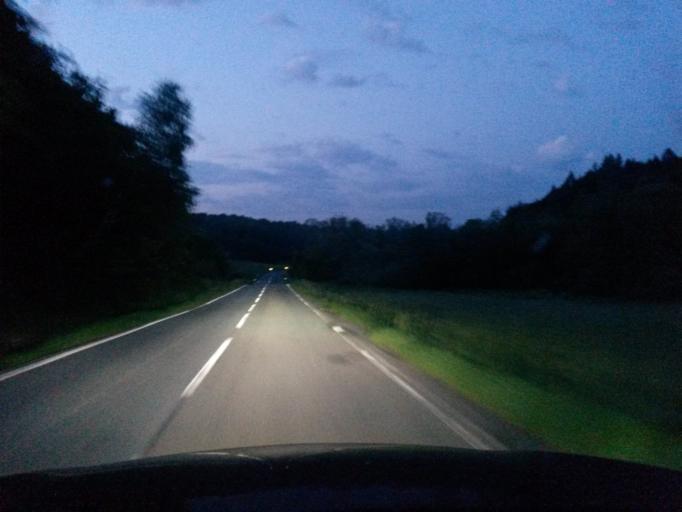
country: UA
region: Zakarpattia
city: Velykyi Bereznyi
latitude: 48.9242
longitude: 22.3261
